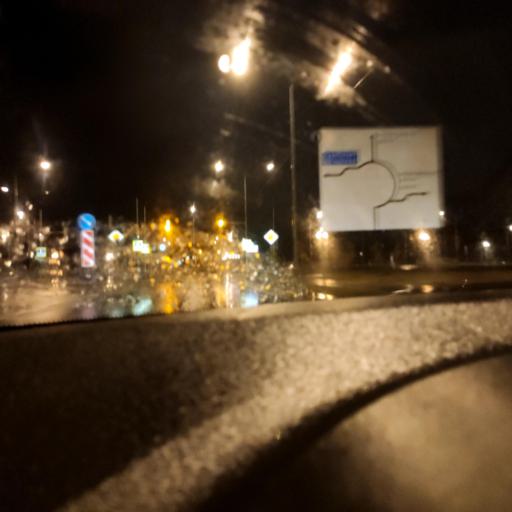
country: RU
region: Samara
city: Petra-Dubrava
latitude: 53.2754
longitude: 50.2631
